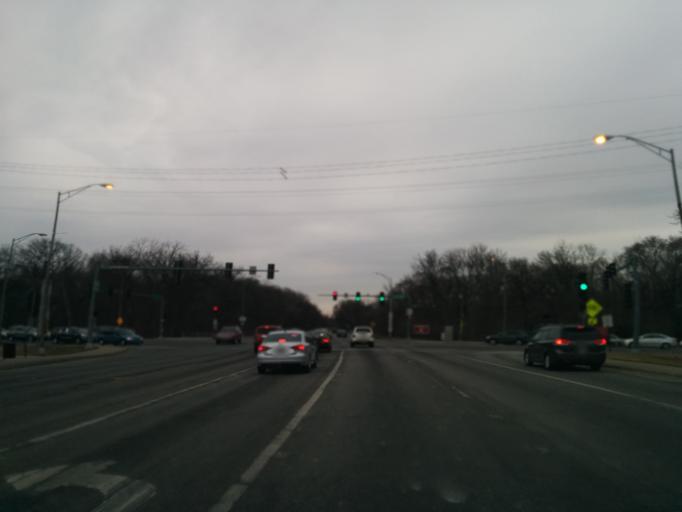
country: US
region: Illinois
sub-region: Cook County
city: Westchester
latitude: 41.8492
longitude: -87.8815
